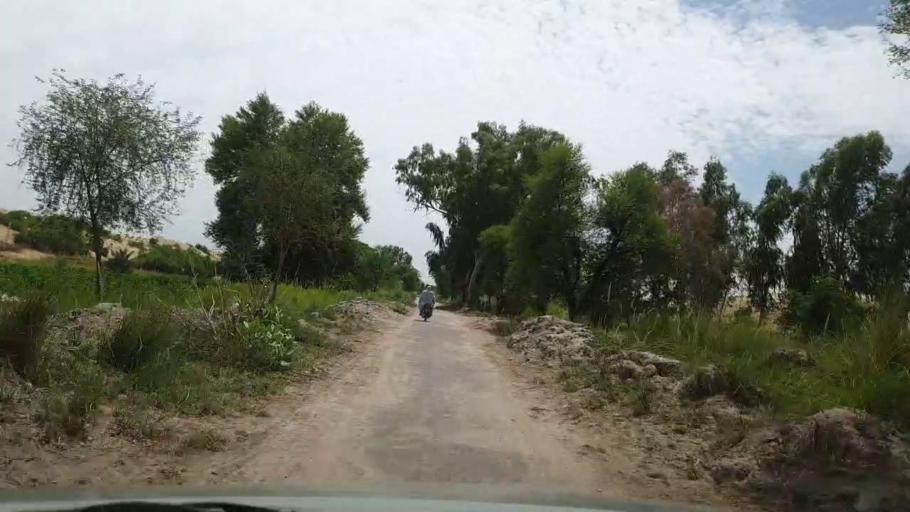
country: PK
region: Sindh
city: Bozdar
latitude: 27.0723
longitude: 68.9689
